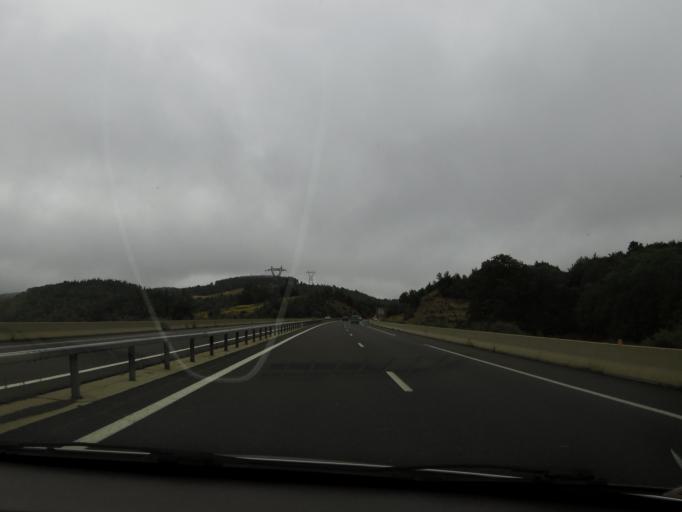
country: FR
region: Languedoc-Roussillon
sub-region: Departement de la Lozere
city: Marvejols
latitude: 44.6140
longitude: 3.2571
